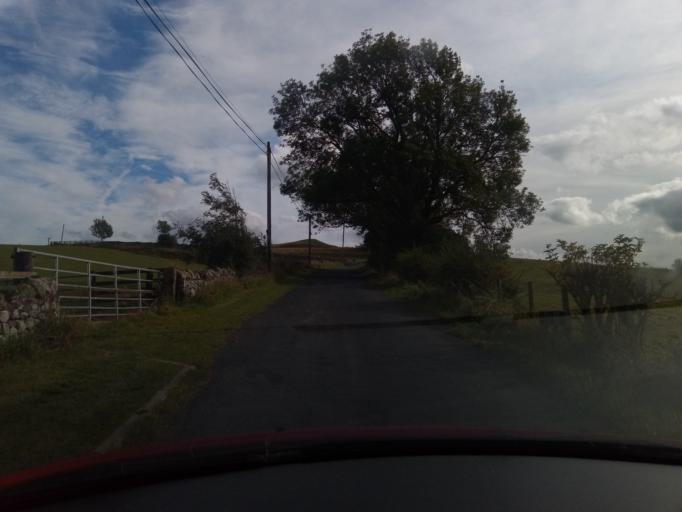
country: GB
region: Scotland
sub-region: The Scottish Borders
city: Kelso
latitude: 55.4780
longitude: -2.3538
